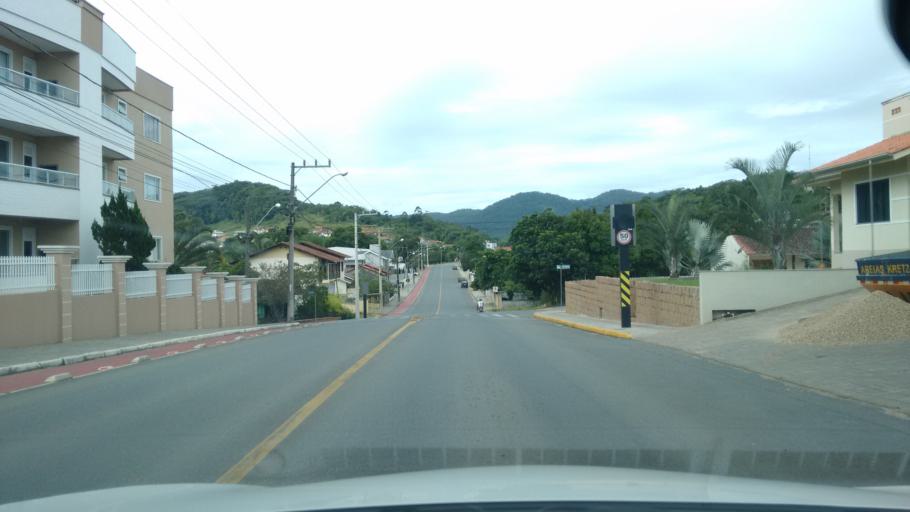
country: BR
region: Santa Catarina
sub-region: Timbo
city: Timbo
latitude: -26.8104
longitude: -49.2676
